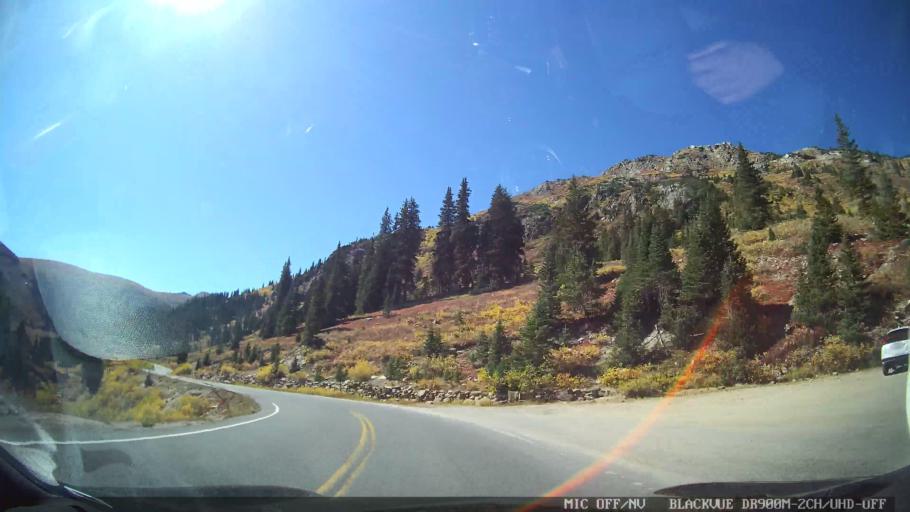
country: US
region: Colorado
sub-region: Pitkin County
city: Aspen
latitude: 39.1249
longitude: -106.5814
